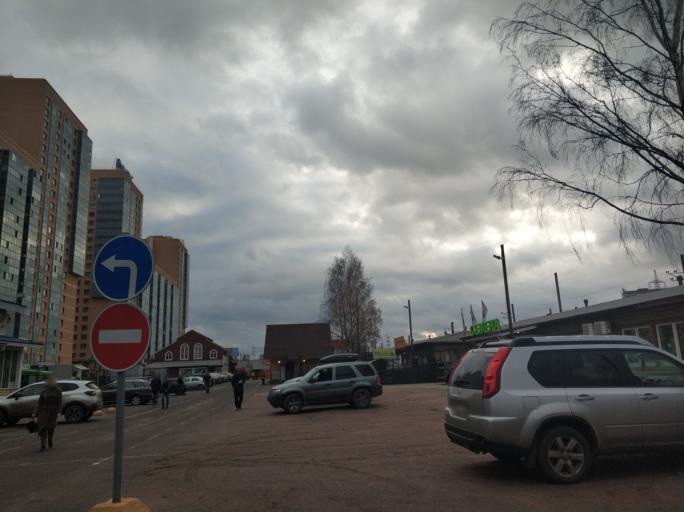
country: RU
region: Leningrad
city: Murino
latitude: 60.0524
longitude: 30.4454
